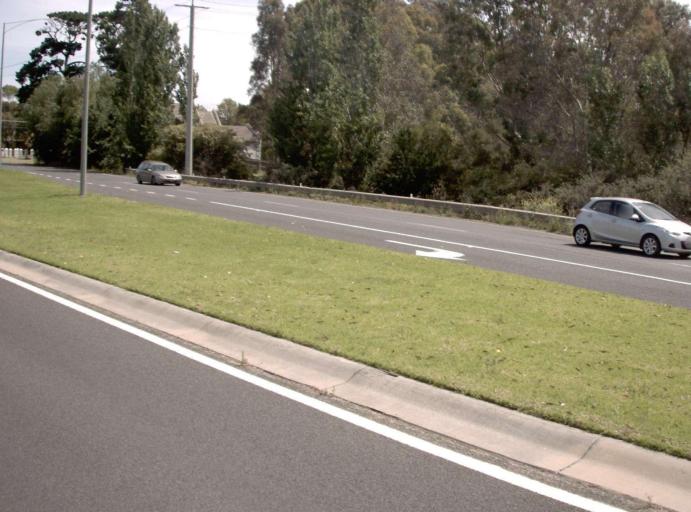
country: AU
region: Victoria
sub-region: Wellington
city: Heyfield
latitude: -38.1492
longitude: 146.7902
